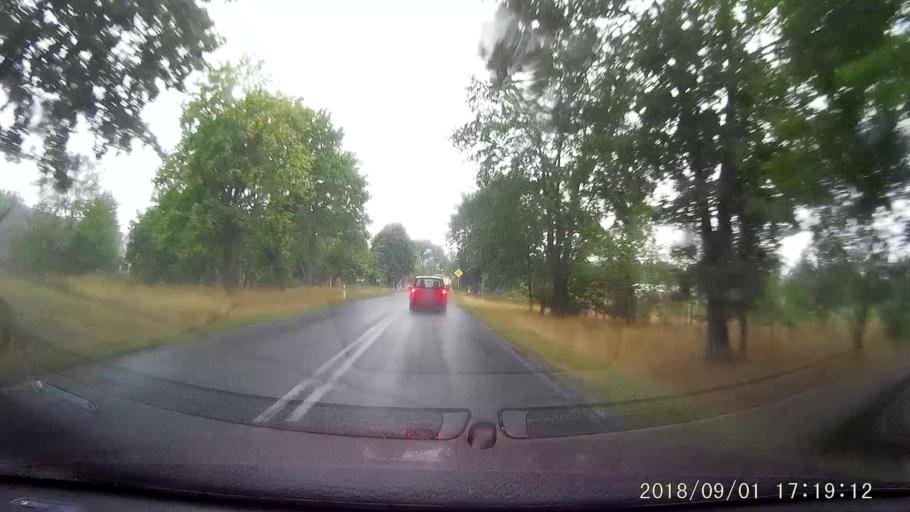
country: PL
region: Lubusz
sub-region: Powiat zielonogorski
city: Nowogrod Bobrzanski
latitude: 51.7329
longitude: 15.2744
